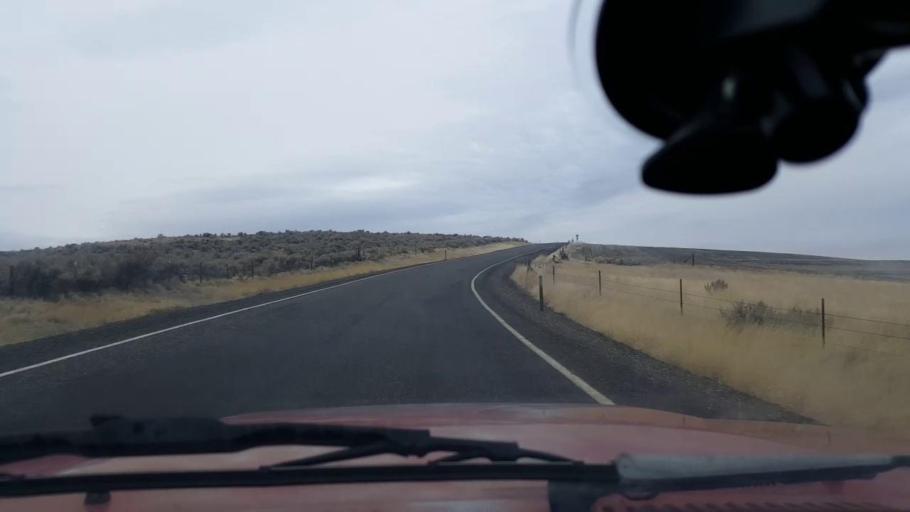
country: US
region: Washington
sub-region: Asotin County
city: Clarkston Heights-Vineland
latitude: 46.3157
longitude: -117.3440
